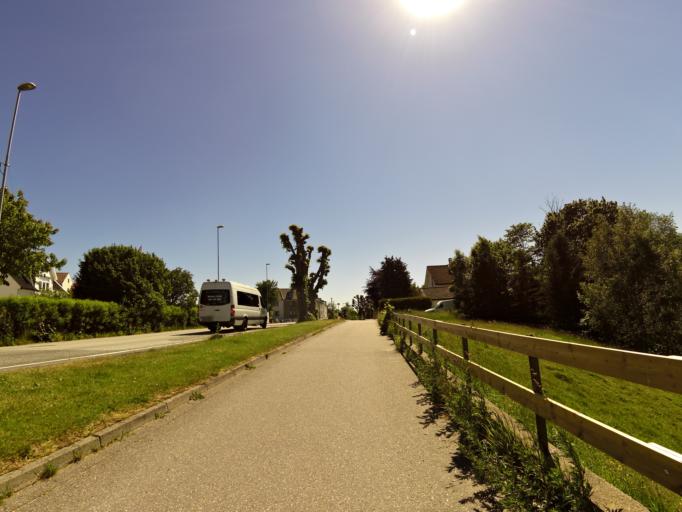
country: NO
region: Vest-Agder
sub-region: Kristiansand
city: Kristiansand
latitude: 58.1559
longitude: 8.0106
